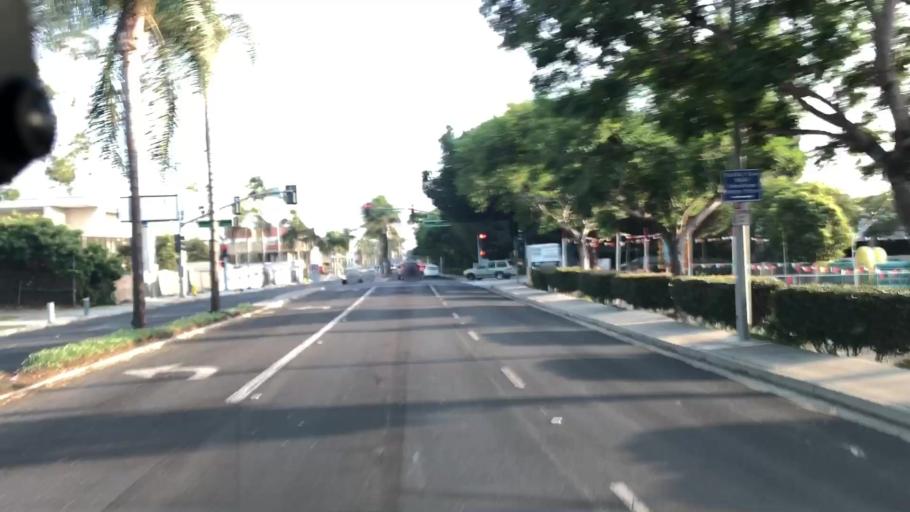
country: US
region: California
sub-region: Ventura County
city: Ventura
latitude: 34.2713
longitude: -119.2474
